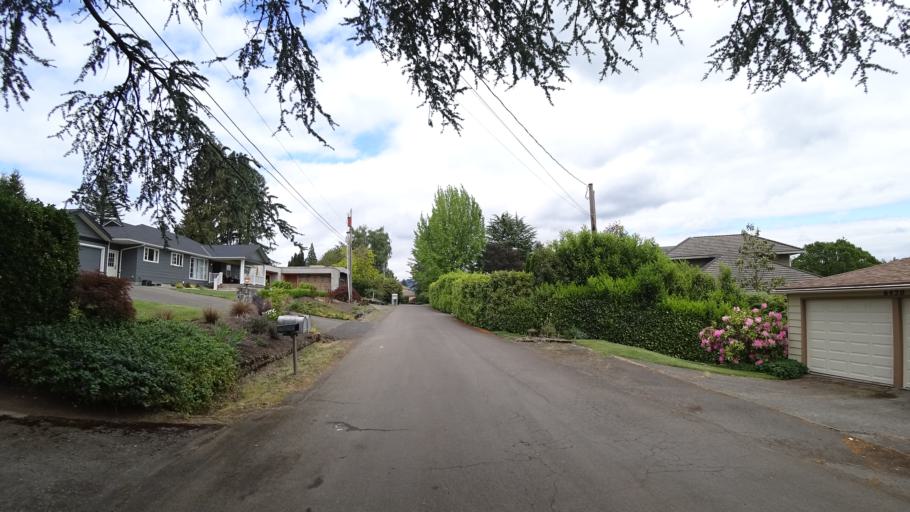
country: US
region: Oregon
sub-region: Washington County
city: Raleigh Hills
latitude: 45.4738
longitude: -122.7677
